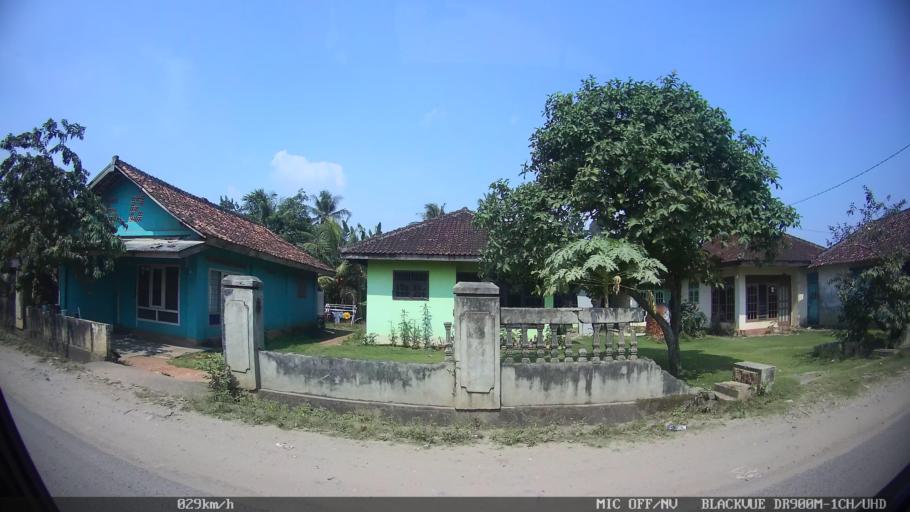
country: ID
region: Lampung
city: Natar
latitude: -5.3080
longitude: 105.2139
